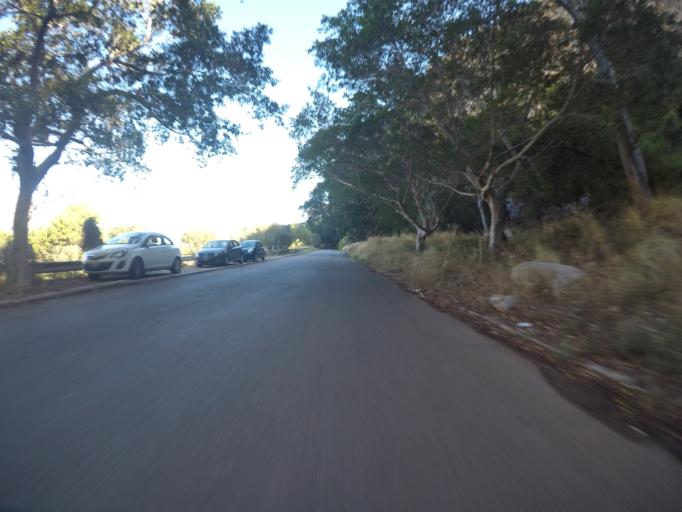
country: IT
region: Sicily
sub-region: Palermo
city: Palermo
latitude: 38.1913
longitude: 13.3371
